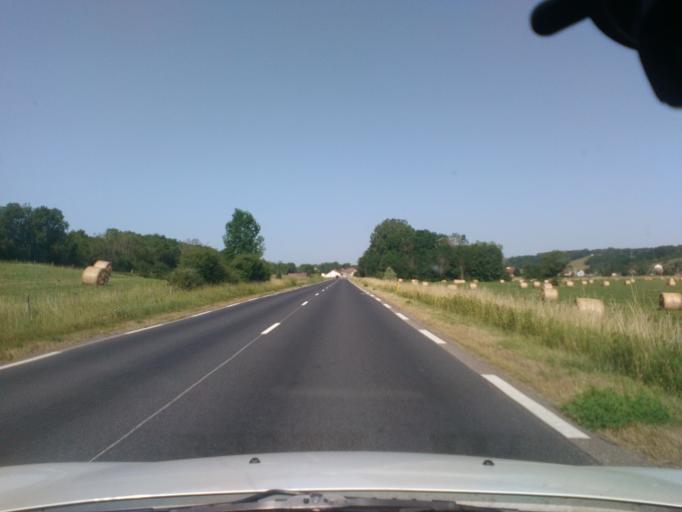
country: FR
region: Lorraine
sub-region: Departement des Vosges
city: Mirecourt
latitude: 48.3077
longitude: 6.1104
